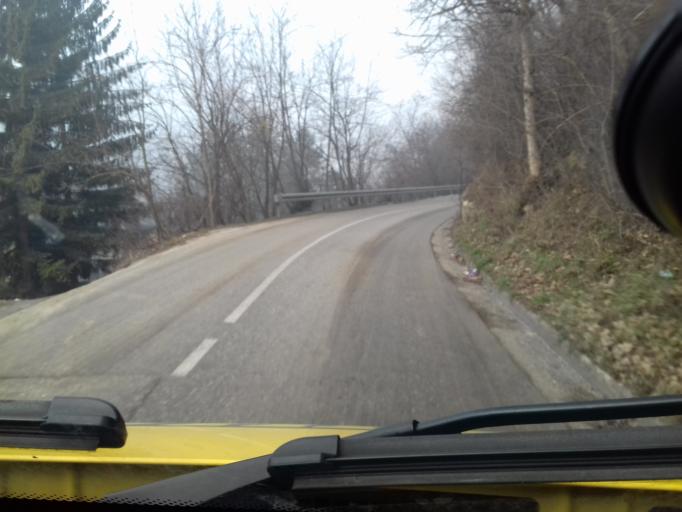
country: BA
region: Federation of Bosnia and Herzegovina
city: Lokvine
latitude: 44.1954
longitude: 17.8748
